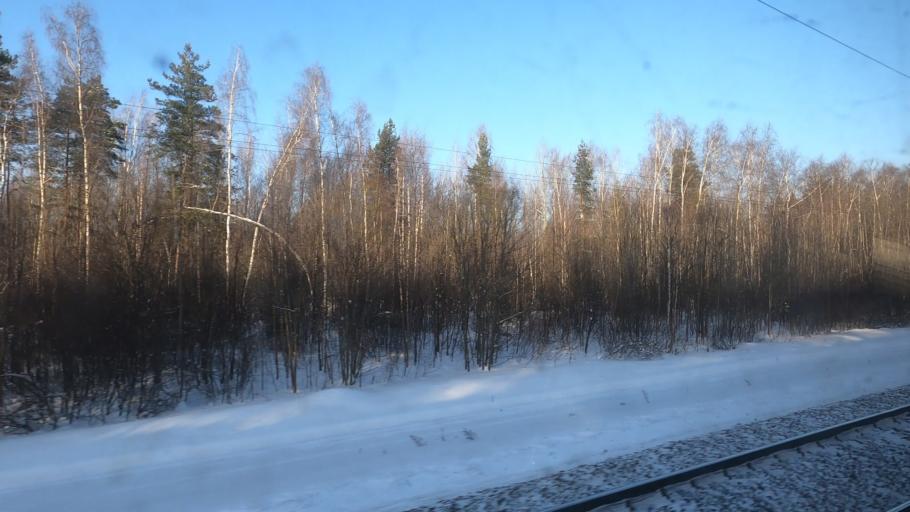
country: RU
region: Moskovskaya
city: Rakhmanovo
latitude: 55.7632
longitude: 38.6020
